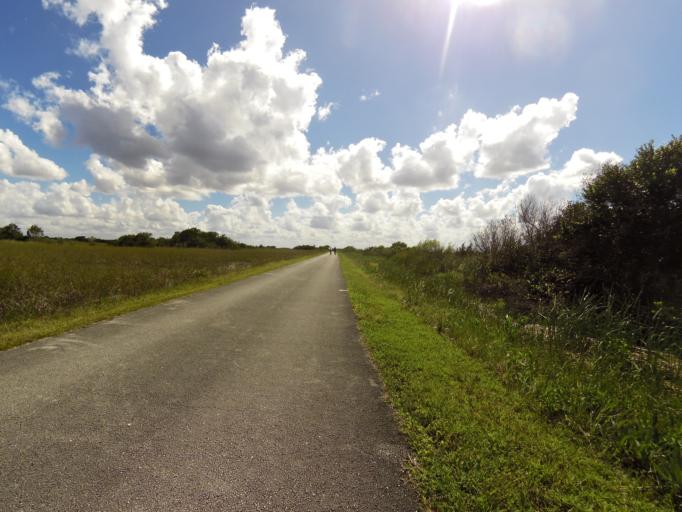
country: US
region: Florida
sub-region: Miami-Dade County
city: The Hammocks
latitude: 25.7003
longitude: -80.7669
